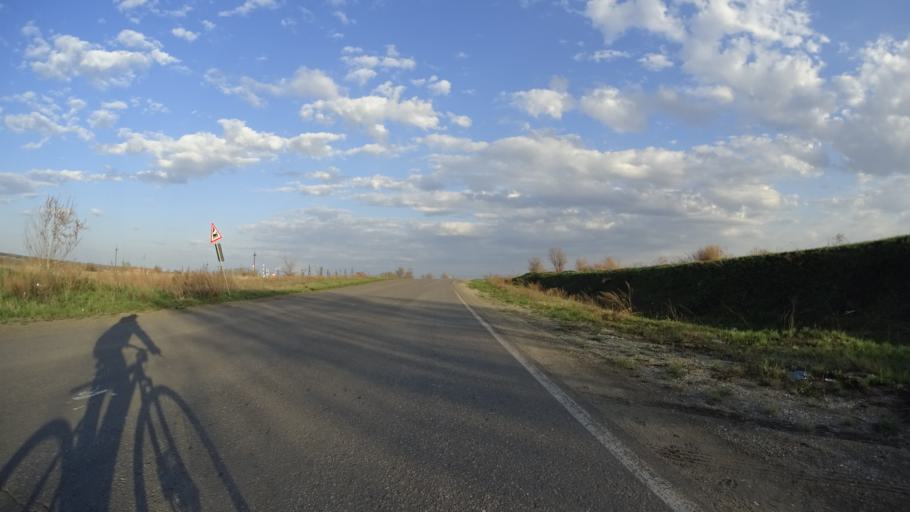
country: RU
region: Chelyabinsk
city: Troitsk
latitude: 54.0620
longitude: 61.5760
